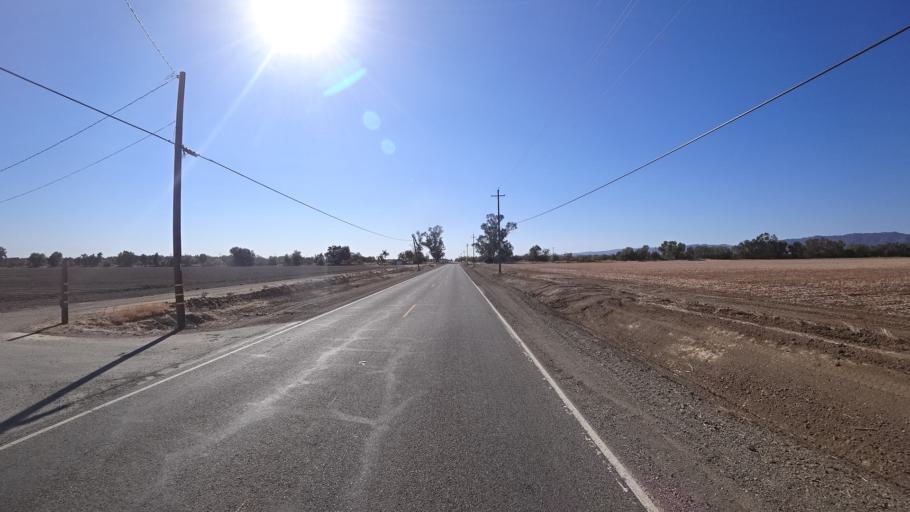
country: US
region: California
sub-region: Yolo County
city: Cottonwood
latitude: 38.6086
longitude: -121.9714
